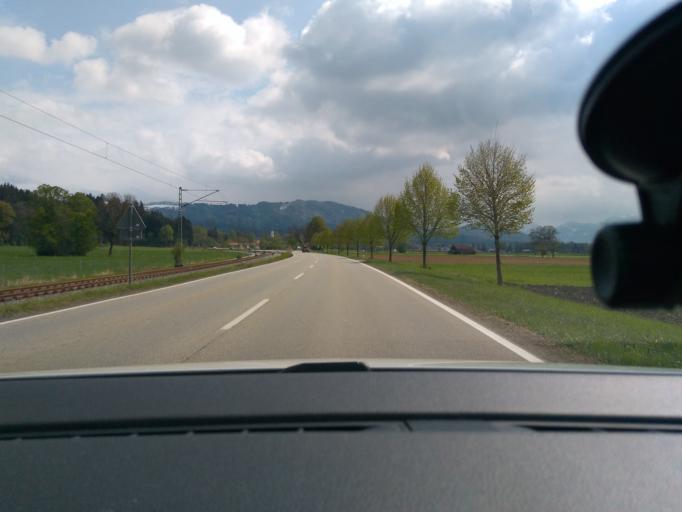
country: DE
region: Bavaria
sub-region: Upper Bavaria
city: Rohrdorf
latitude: 47.8116
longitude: 12.1607
